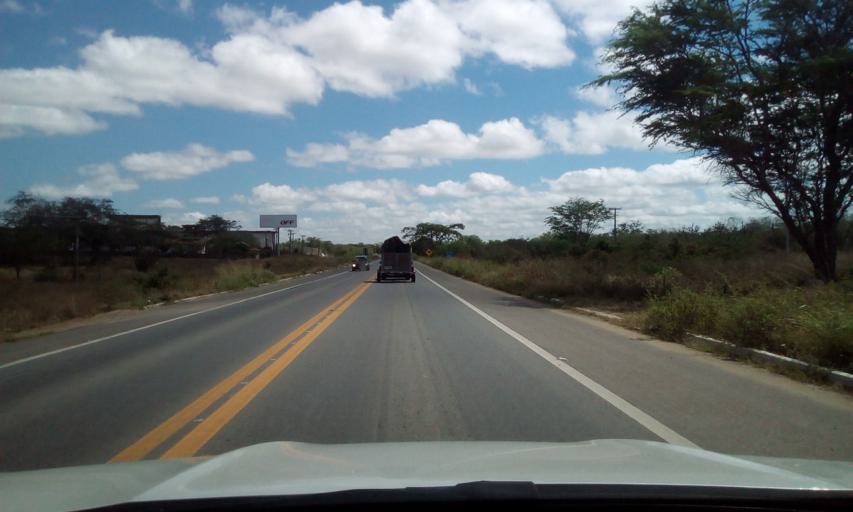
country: BR
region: Paraiba
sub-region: Campina Grande
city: Campina Grande
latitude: -7.3272
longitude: -35.8968
